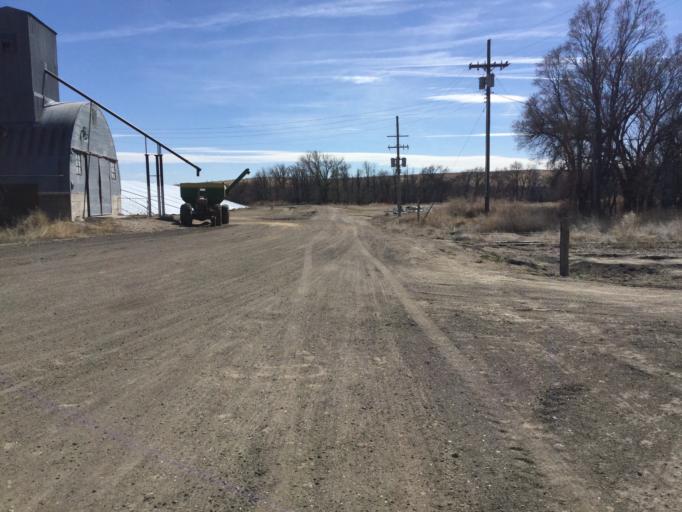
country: US
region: Kansas
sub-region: Decatur County
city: Oberlin
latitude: 39.9059
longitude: -100.7841
